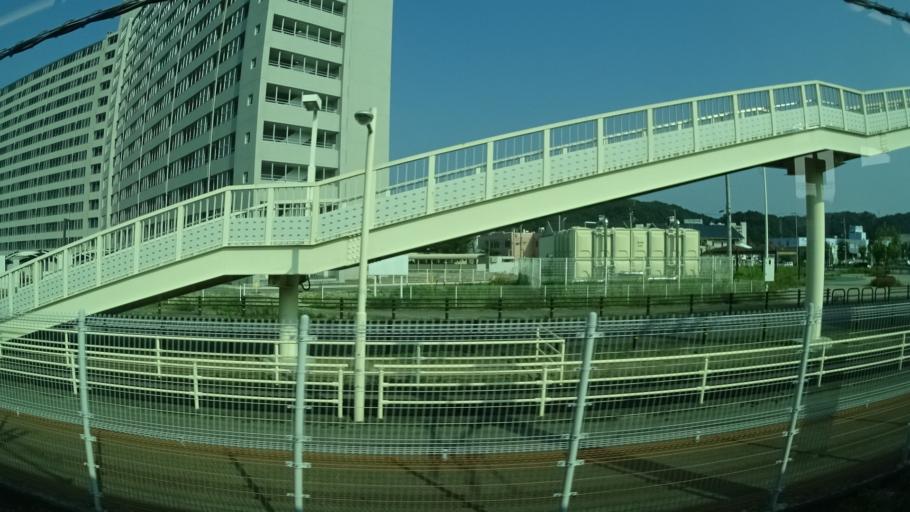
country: JP
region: Fukushima
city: Iwaki
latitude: 37.0461
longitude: 140.8646
